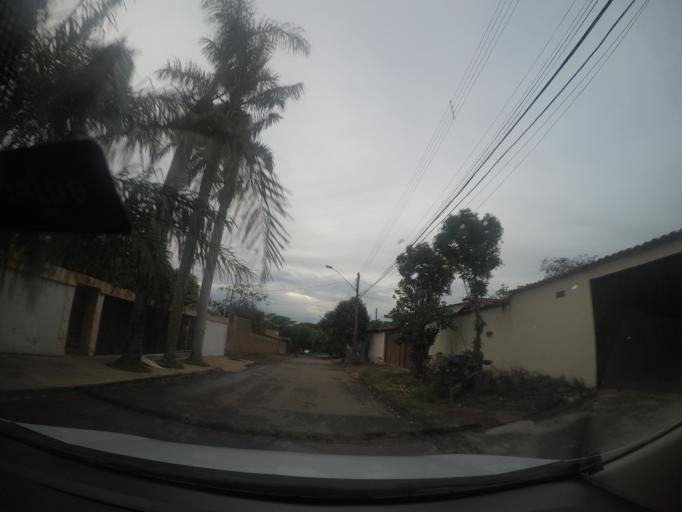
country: BR
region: Goias
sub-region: Goiania
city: Goiania
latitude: -16.6344
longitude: -49.2395
